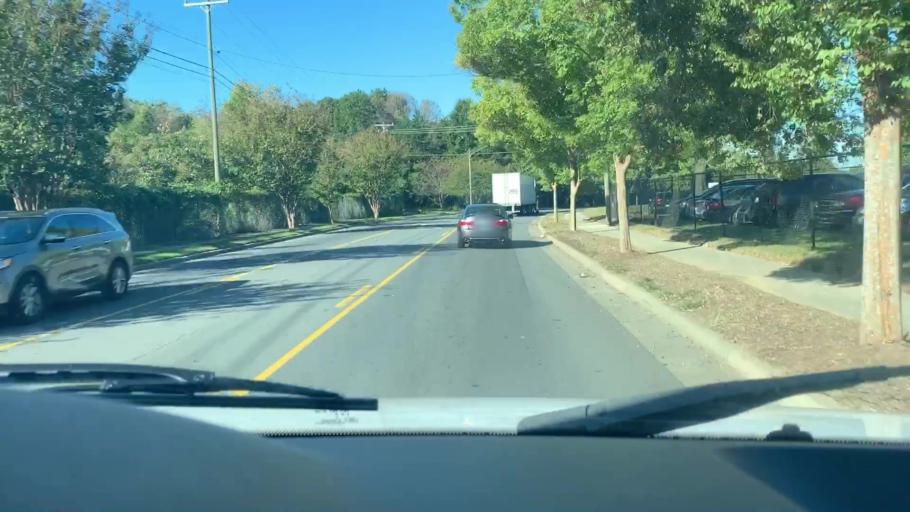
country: US
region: North Carolina
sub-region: Mecklenburg County
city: Charlotte
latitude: 35.2616
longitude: -80.8254
